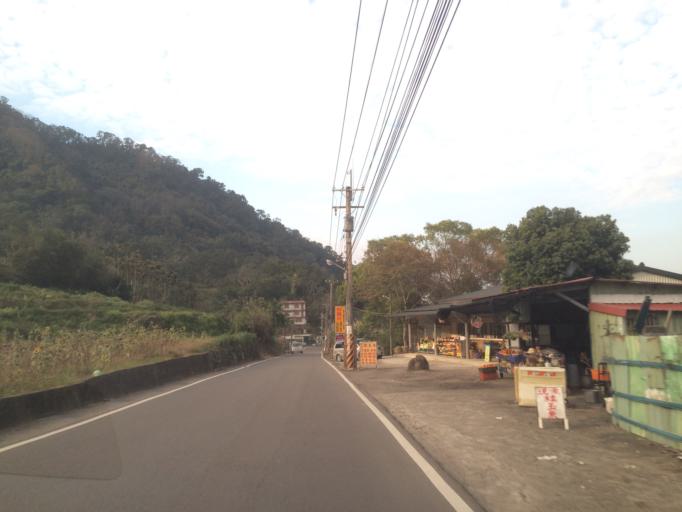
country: TW
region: Taiwan
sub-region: Hsinchu
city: Hsinchu
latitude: 24.6839
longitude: 121.1016
